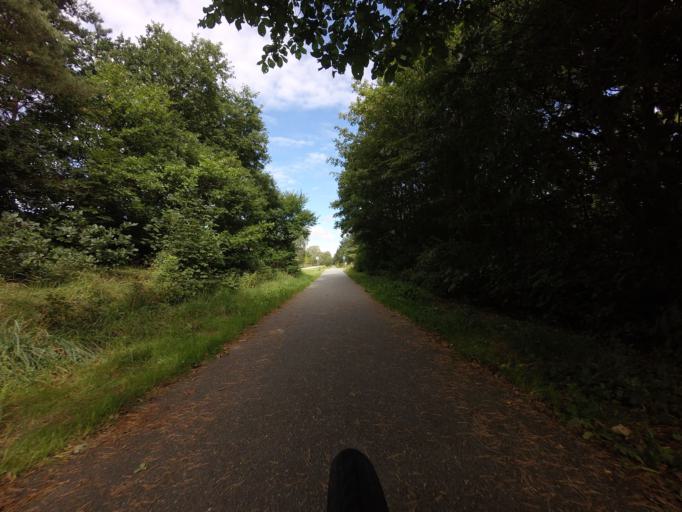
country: DK
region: Central Jutland
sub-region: Norddjurs Kommune
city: Auning
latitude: 56.4336
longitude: 10.3739
